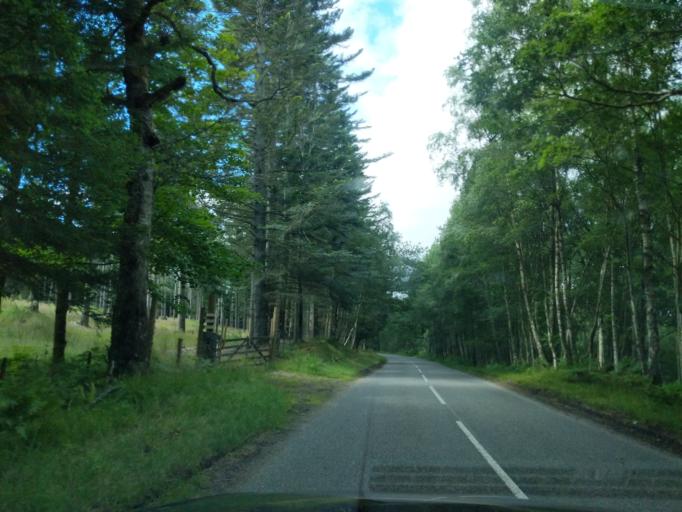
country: GB
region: Scotland
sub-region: Aberdeenshire
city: Ballater
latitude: 57.0641
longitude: -2.9161
